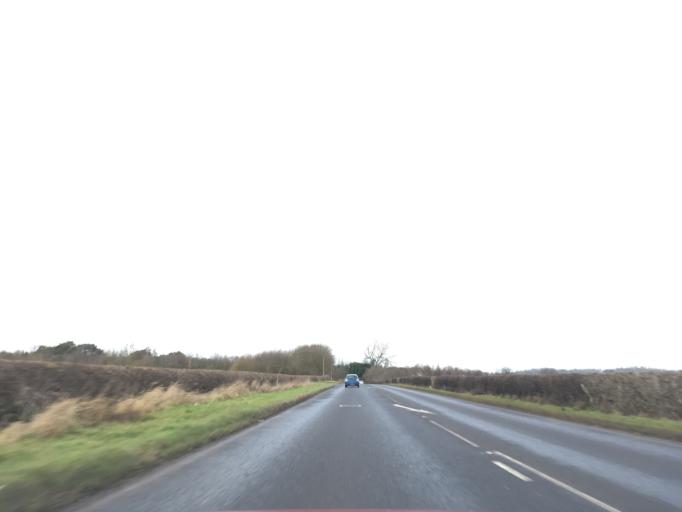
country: GB
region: England
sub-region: Nottinghamshire
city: Ruddington
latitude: 52.8815
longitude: -1.1352
